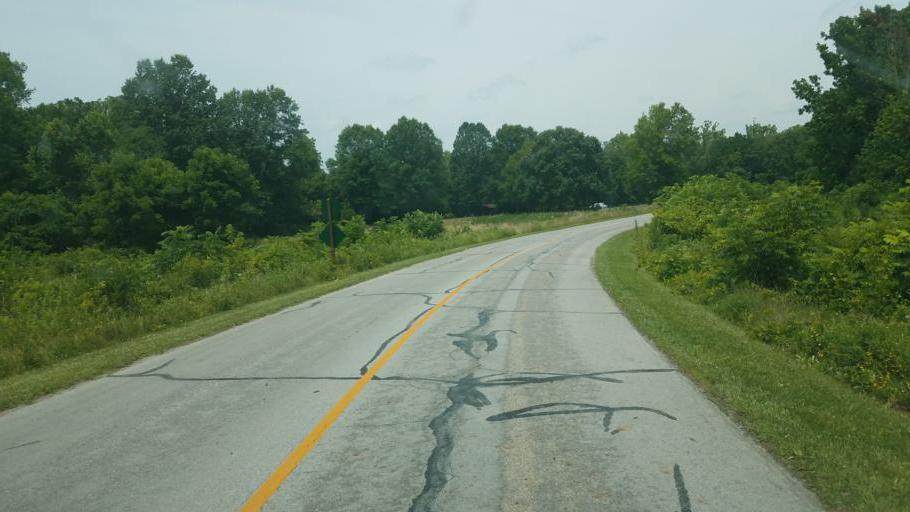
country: US
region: Ohio
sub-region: Delaware County
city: Powell
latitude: 40.1482
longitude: -83.0390
